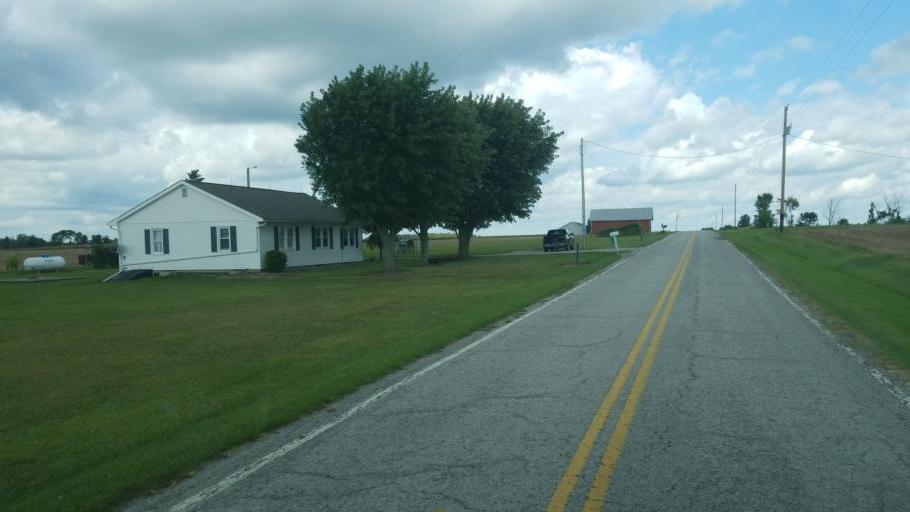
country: US
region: Ohio
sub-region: Huron County
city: Willard
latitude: 41.1205
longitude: -82.7552
